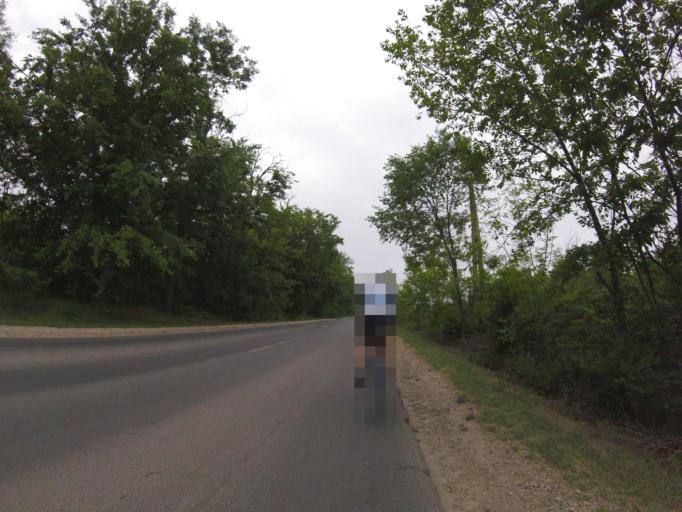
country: HU
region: Pest
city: Bugyi
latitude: 47.2286
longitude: 19.1776
